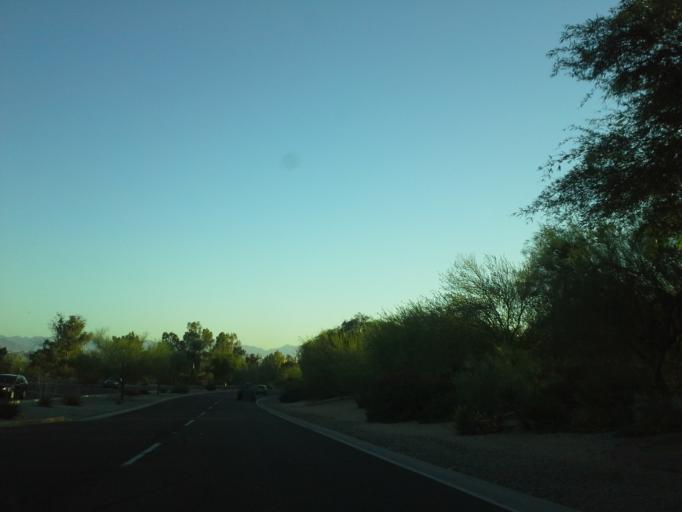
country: US
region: Arizona
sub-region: Maricopa County
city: Paradise Valley
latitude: 33.5309
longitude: -112.0153
